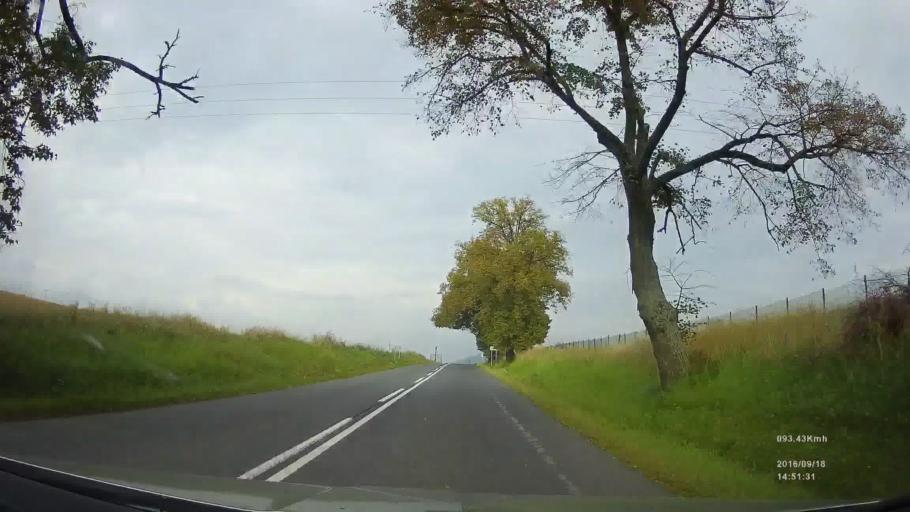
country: SK
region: Presovsky
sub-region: Okres Presov
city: Levoca
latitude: 49.0097
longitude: 20.5856
